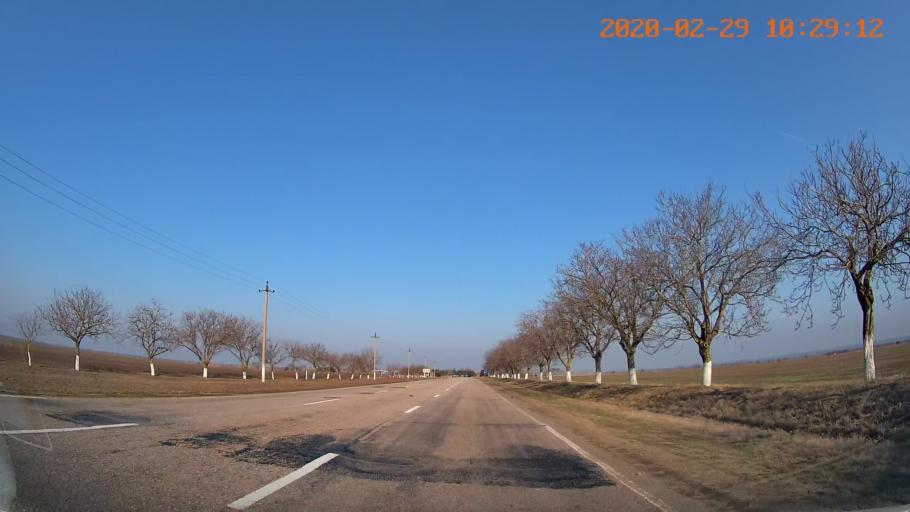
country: MD
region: Telenesti
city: Tiraspolul Nou
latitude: 46.9205
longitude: 29.5871
